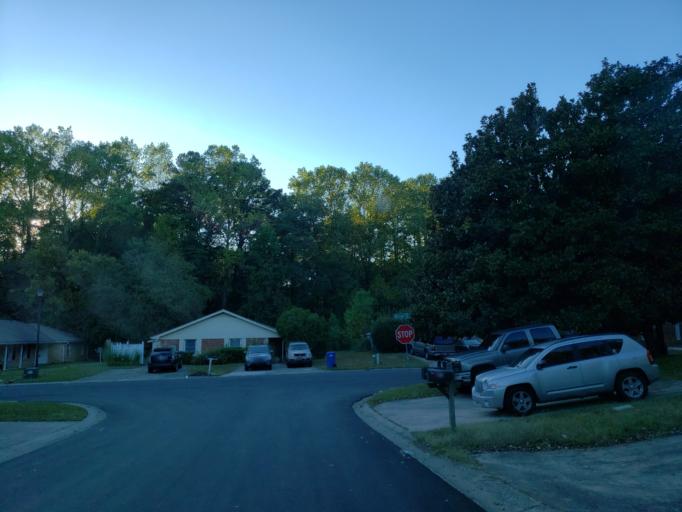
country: US
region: Georgia
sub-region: Cobb County
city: Marietta
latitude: 33.9492
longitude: -84.5760
